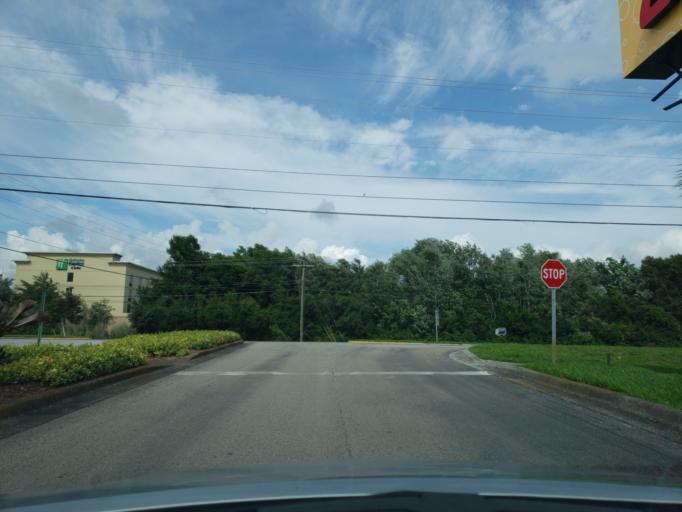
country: US
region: Florida
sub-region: Hillsborough County
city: Egypt Lake-Leto
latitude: 28.0340
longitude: -82.5417
